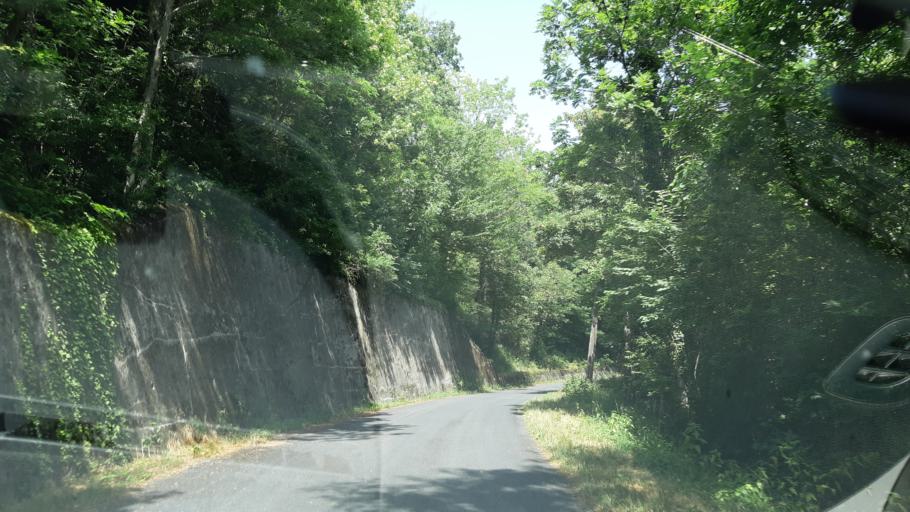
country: FR
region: Languedoc-Roussillon
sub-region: Departement des Pyrenees-Orientales
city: Arles
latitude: 42.5443
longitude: 2.5877
